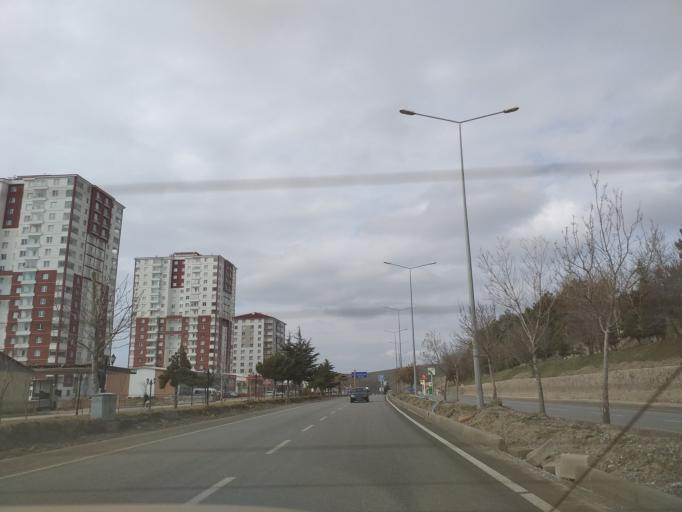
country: TR
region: Yozgat
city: Yozgat
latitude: 39.8180
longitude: 34.7939
